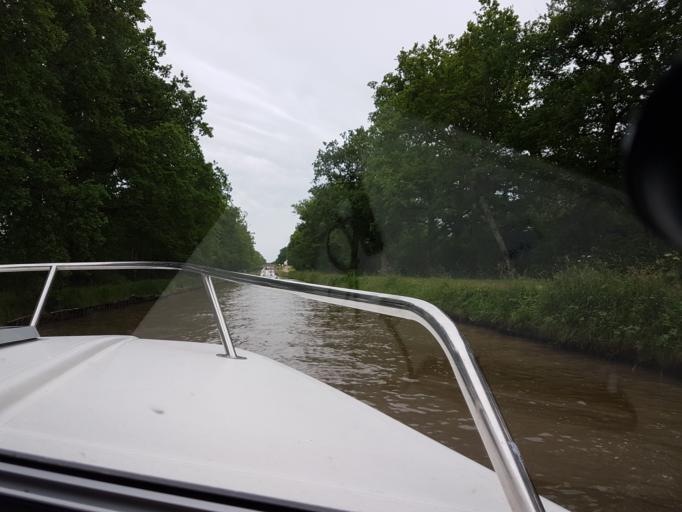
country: FR
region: Bourgogne
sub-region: Departement de la Nievre
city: Clamecy
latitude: 47.3820
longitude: 3.6022
